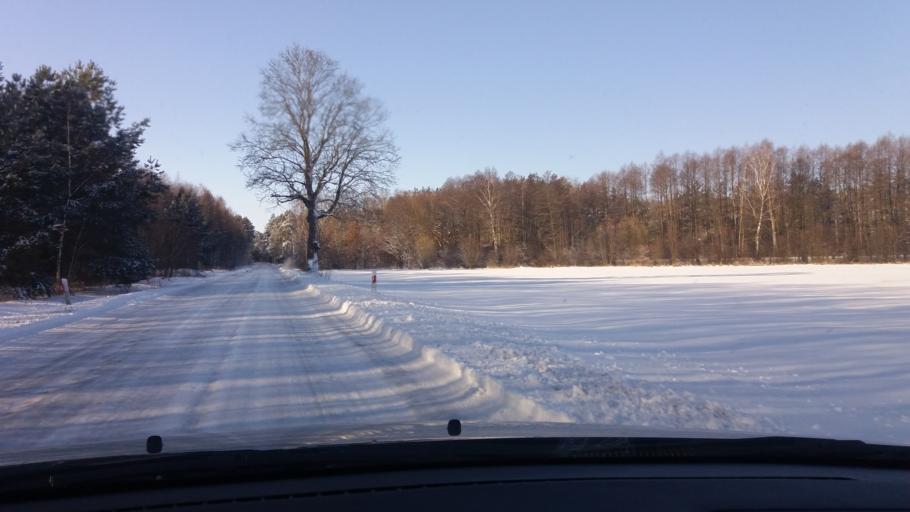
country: PL
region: Masovian Voivodeship
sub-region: Powiat mlawski
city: Dzierzgowo
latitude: 53.3311
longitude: 20.6485
